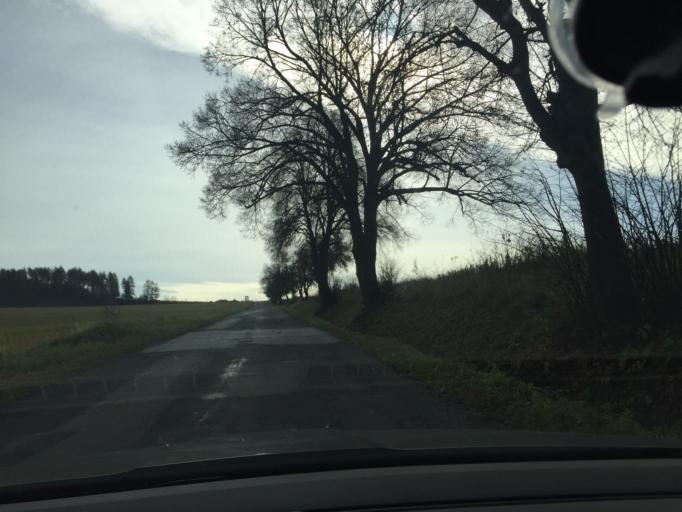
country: SK
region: Presovsky
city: Spisske Podhradie
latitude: 49.0026
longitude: 20.7770
